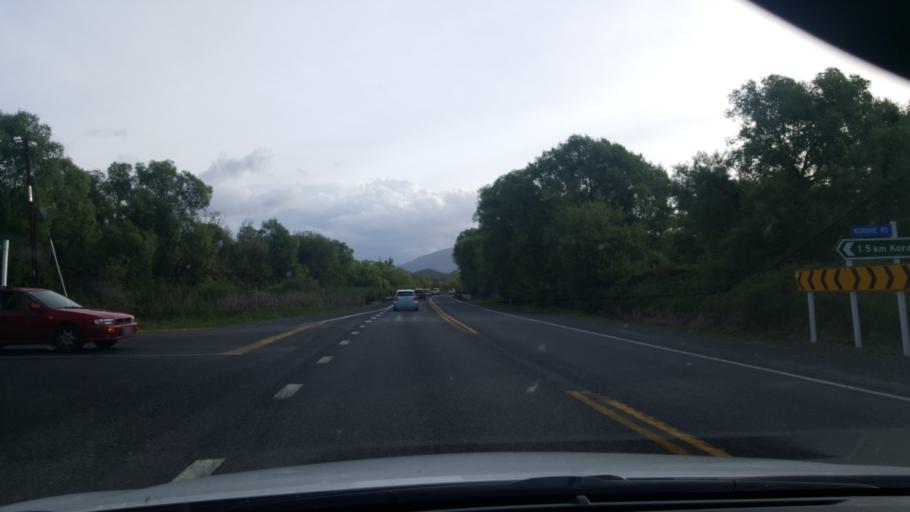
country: NZ
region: Waikato
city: Turangi
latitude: -38.9486
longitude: 175.8499
